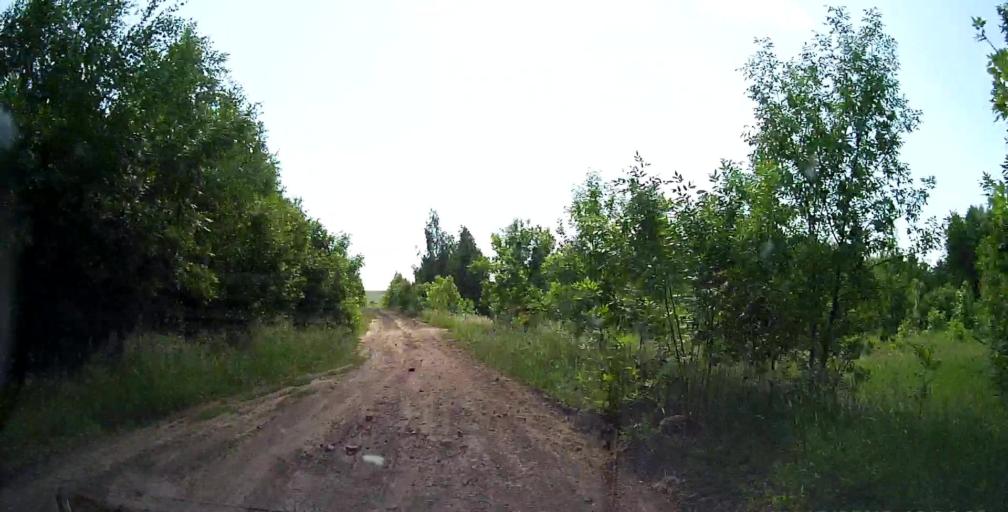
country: RU
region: Tula
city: Kurkino
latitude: 53.1684
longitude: 38.4877
